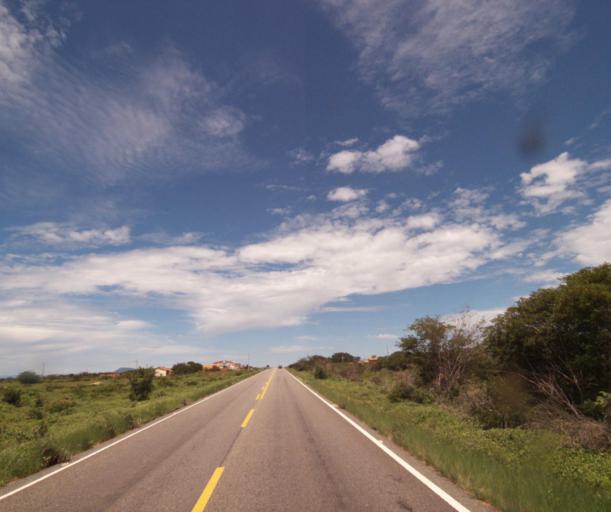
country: BR
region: Bahia
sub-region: Palmas De Monte Alto
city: Palmas de Monte Alto
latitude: -14.2476
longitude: -43.1392
